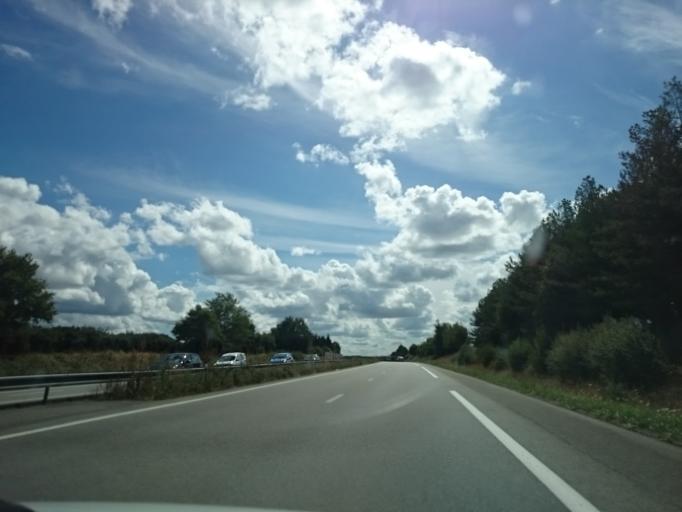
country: FR
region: Pays de la Loire
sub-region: Departement de la Loire-Atlantique
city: Mauves-sur-Loire
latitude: 47.3256
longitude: -1.4050
